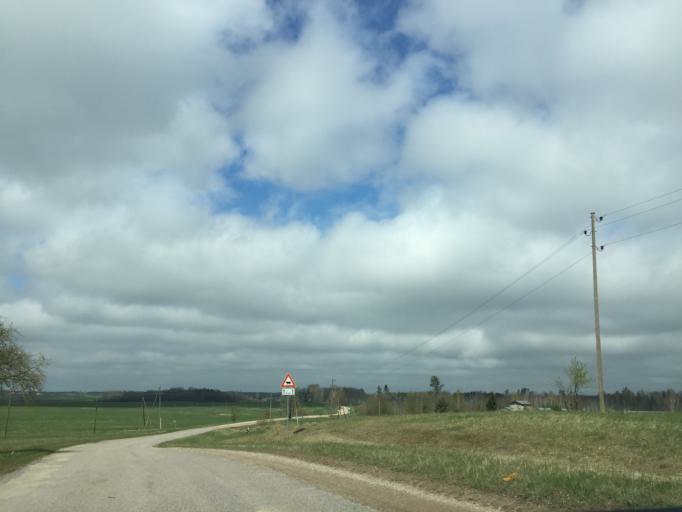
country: EE
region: Valgamaa
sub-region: Valga linn
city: Valga
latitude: 57.5538
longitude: 26.2850
